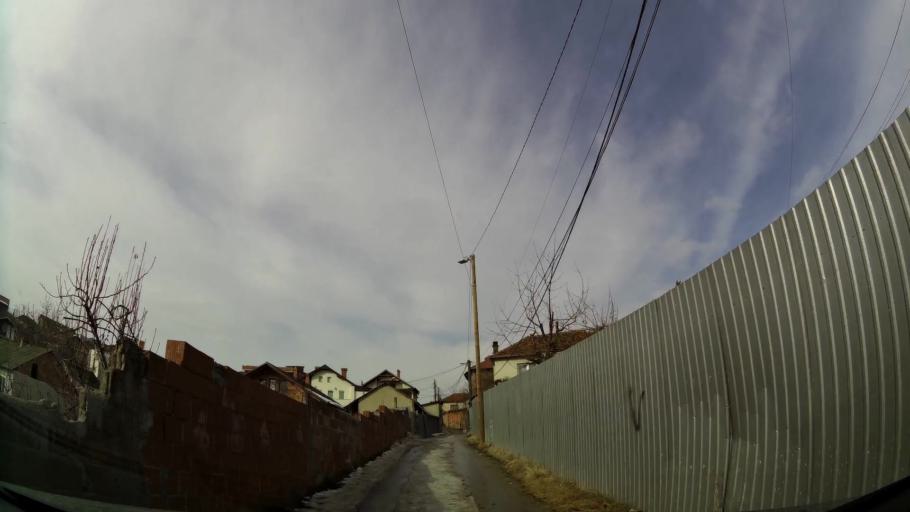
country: XK
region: Pristina
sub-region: Komuna e Prishtines
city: Pristina
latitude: 42.6814
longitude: 21.1717
